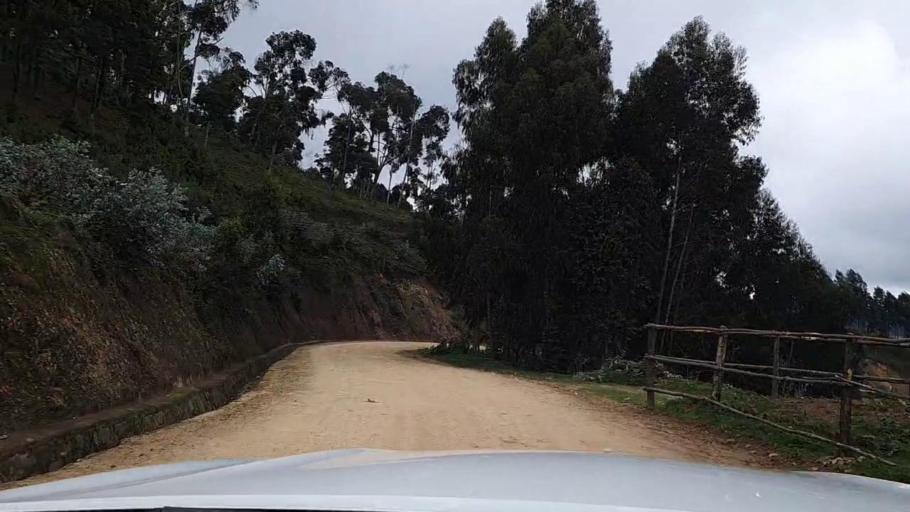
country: RW
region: Southern Province
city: Nzega
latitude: -2.3798
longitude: 29.3835
